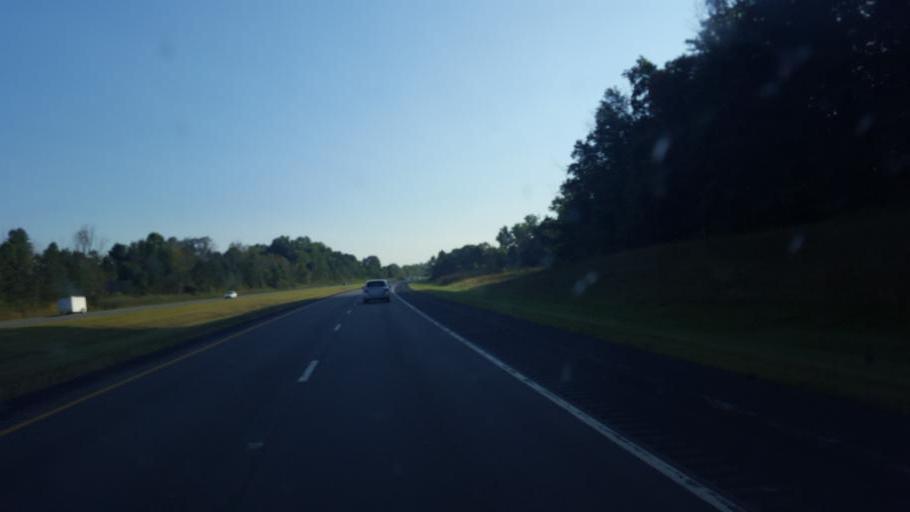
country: US
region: Ohio
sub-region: Medina County
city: Brunswick
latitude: 41.1831
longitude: -81.7567
